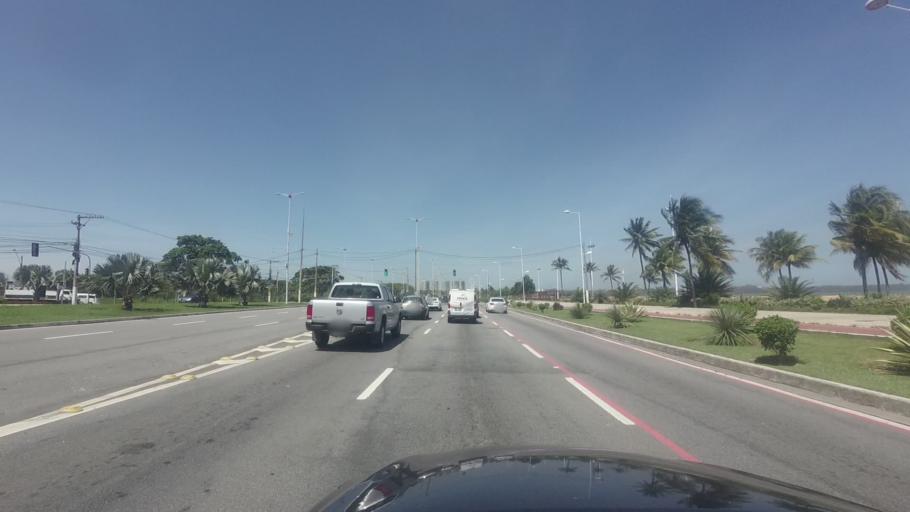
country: BR
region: Espirito Santo
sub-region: Vila Velha
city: Vila Velha
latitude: -20.2750
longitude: -40.2825
